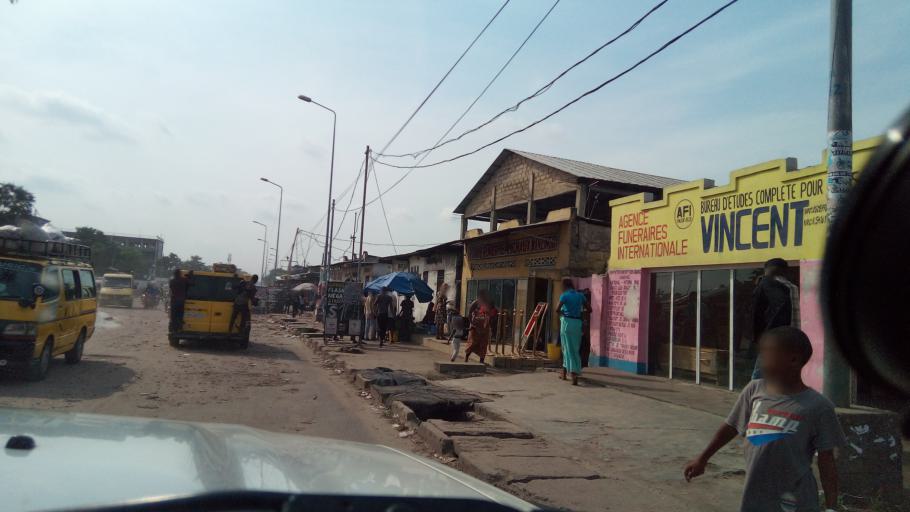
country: CD
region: Kinshasa
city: Kinshasa
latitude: -4.3479
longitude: 15.3153
